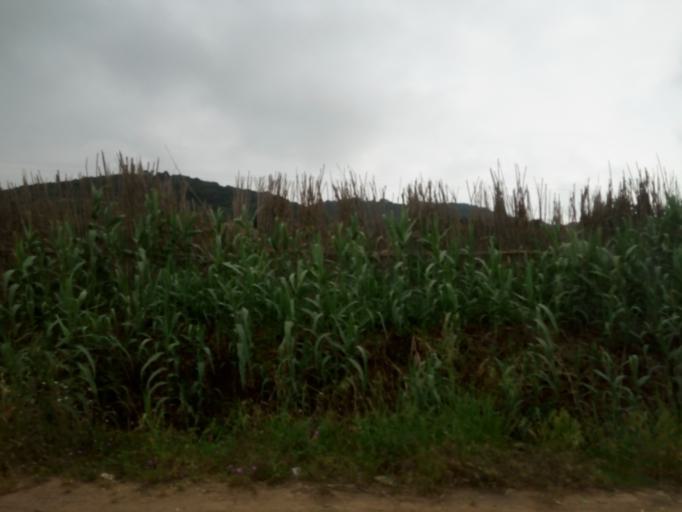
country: DZ
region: Tipaza
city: Tipasa
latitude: 36.5898
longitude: 2.5225
